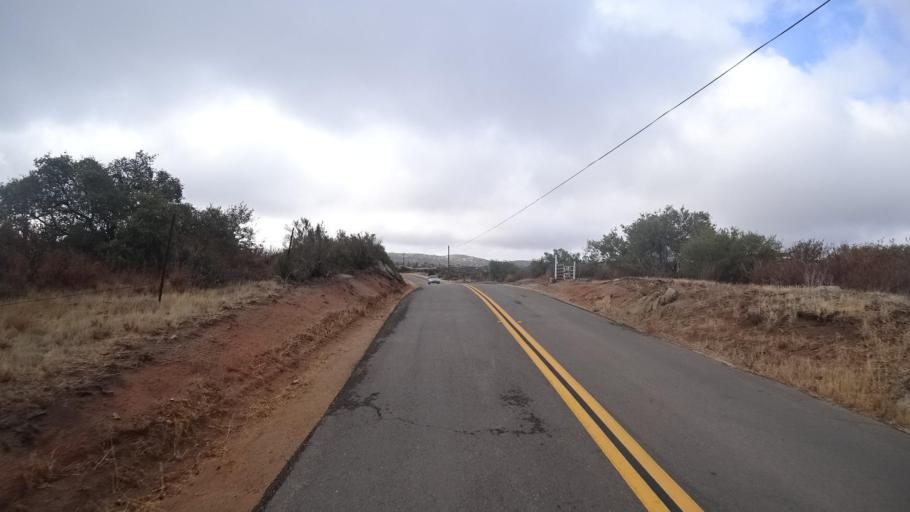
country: MX
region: Baja California
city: Tecate
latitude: 32.6085
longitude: -116.5769
